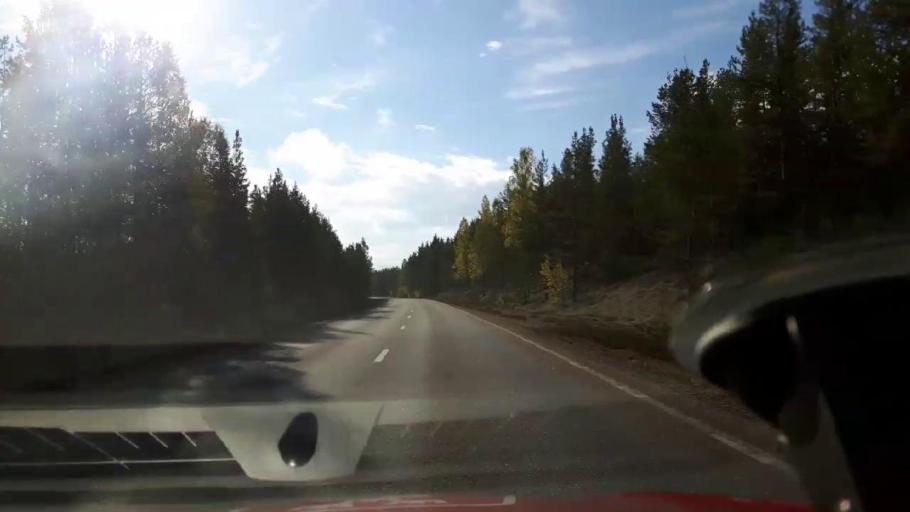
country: SE
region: Vaesternorrland
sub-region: Ange Kommun
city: Ange
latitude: 62.0706
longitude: 15.1036
